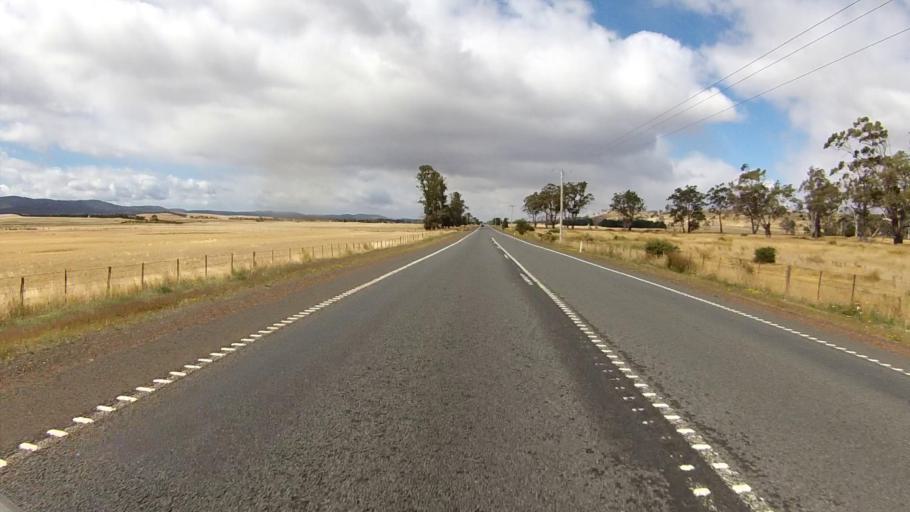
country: AU
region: Tasmania
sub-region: Northern Midlands
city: Evandale
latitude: -41.9552
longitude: 147.4964
